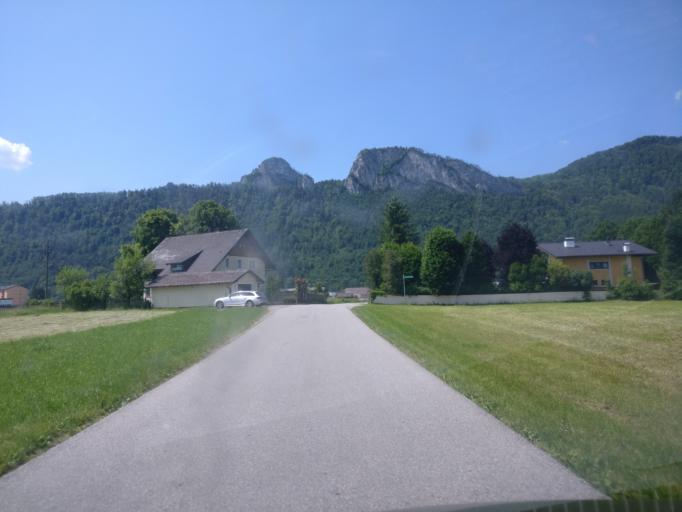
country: AT
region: Salzburg
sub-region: Politischer Bezirk Hallein
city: Oberalm
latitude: 47.6981
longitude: 13.0918
